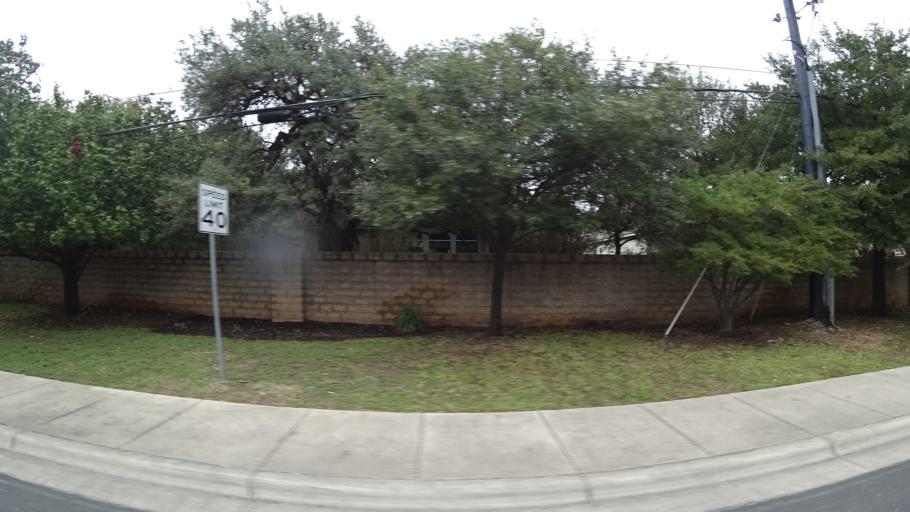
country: US
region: Texas
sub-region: Williamson County
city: Anderson Mill
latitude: 30.4497
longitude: -97.8165
